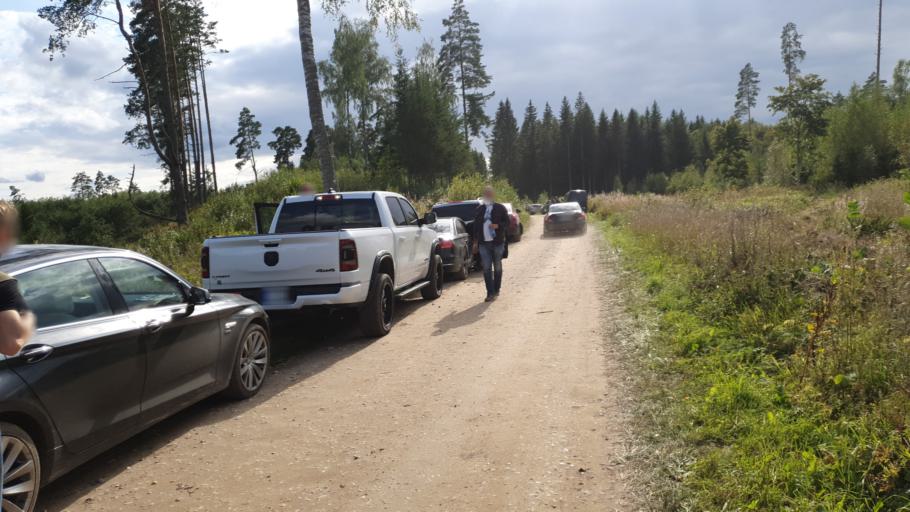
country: EE
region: Tartu
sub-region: UElenurme vald
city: Ulenurme
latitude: 58.1288
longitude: 26.7447
